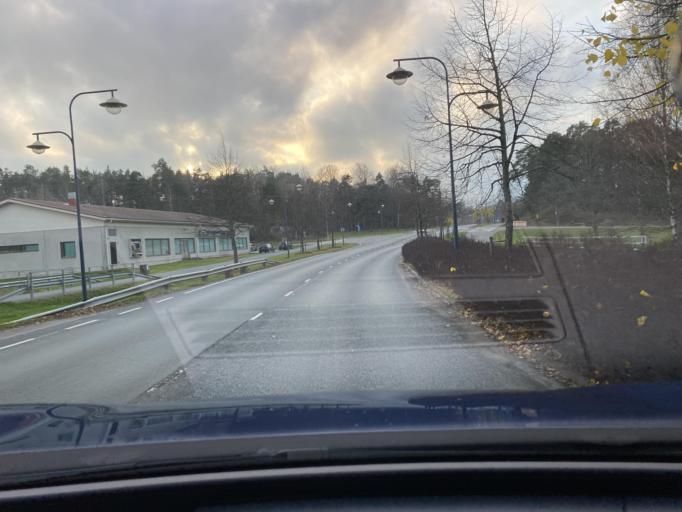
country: FI
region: Varsinais-Suomi
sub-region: Turku
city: Naantali
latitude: 60.4742
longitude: 22.0391
